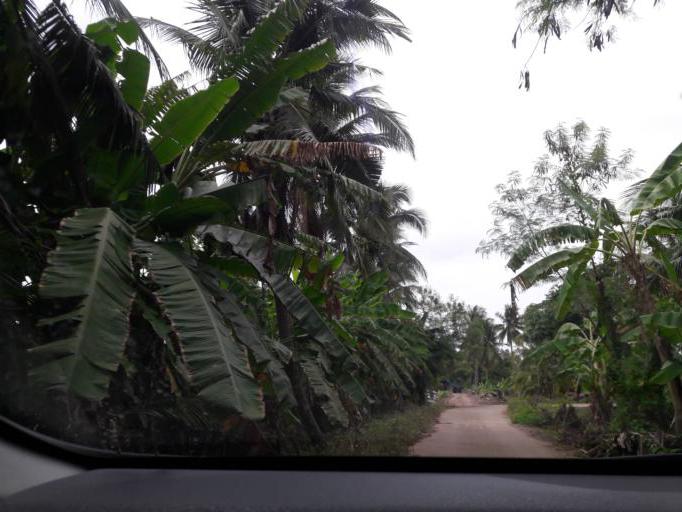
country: TH
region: Ratchaburi
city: Damnoen Saduak
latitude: 13.5647
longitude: 99.9897
